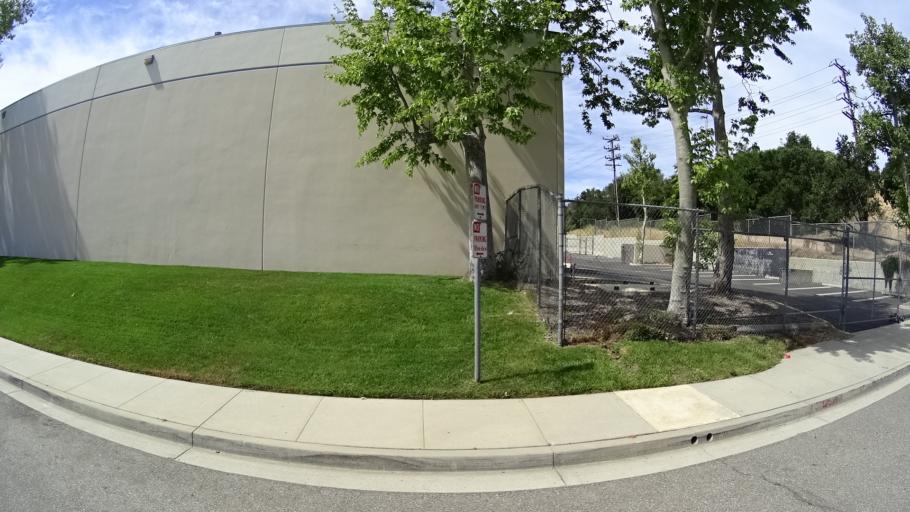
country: US
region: California
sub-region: Ventura County
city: Casa Conejo
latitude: 34.1982
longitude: -118.9291
